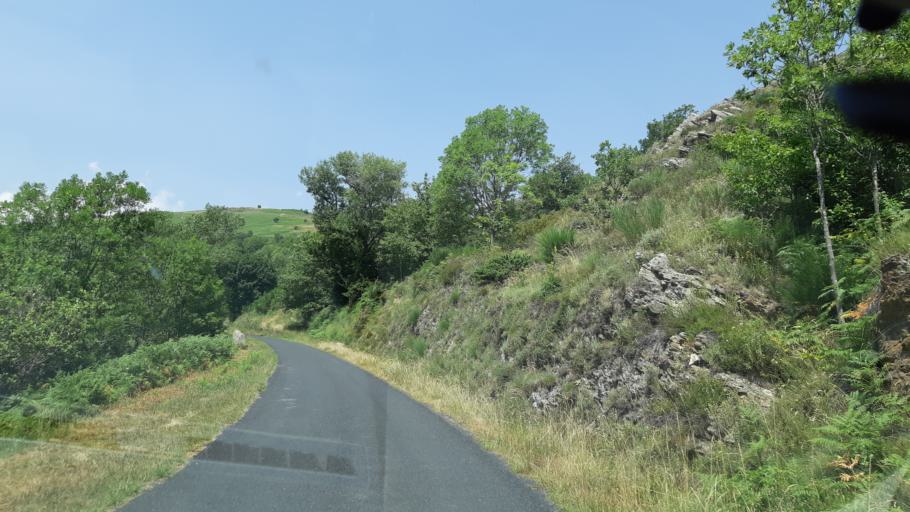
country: FR
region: Languedoc-Roussillon
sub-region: Departement des Pyrenees-Orientales
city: Arles
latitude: 42.5409
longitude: 2.5753
